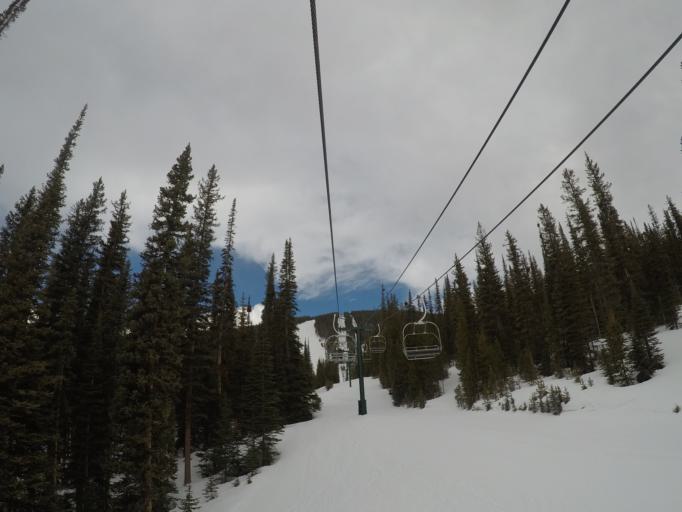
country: US
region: Montana
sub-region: Granite County
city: Philipsburg
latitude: 46.2508
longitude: -113.2408
